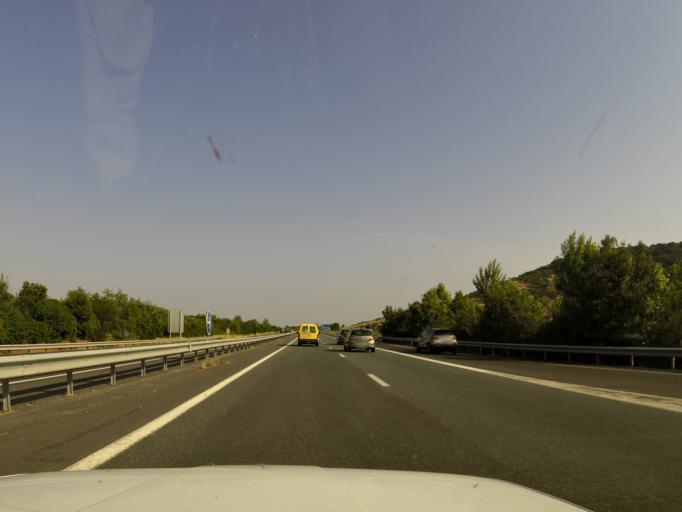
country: FR
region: Languedoc-Roussillon
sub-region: Departement de l'Herault
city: Nebian
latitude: 43.6720
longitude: 3.4259
